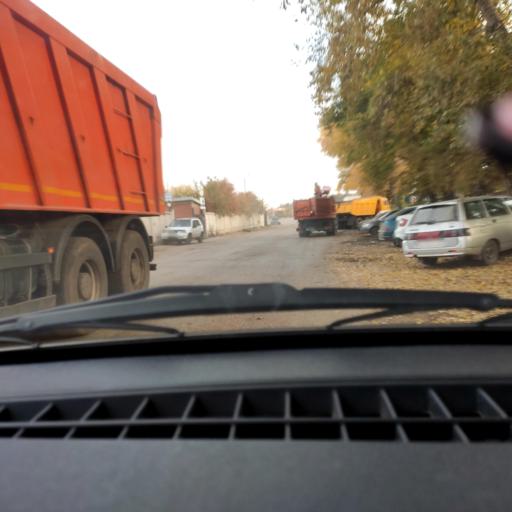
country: RU
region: Bashkortostan
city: Ufa
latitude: 54.7511
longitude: 55.9806
